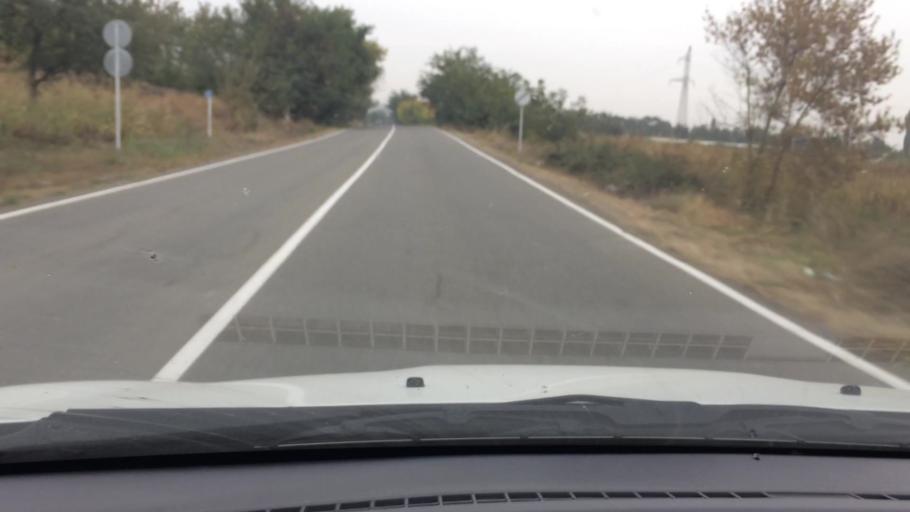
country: GE
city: Naghvarevi
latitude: 41.3172
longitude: 44.7940
